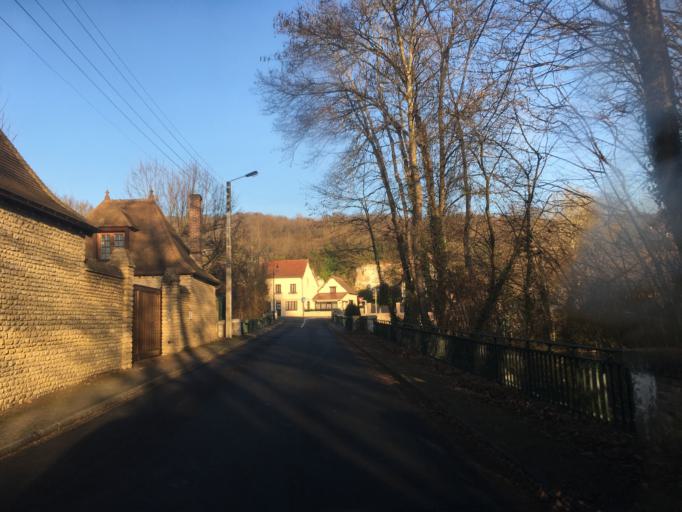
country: FR
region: Haute-Normandie
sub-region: Departement de l'Eure
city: Houlbec-Cocherel
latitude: 49.0569
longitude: 1.3334
